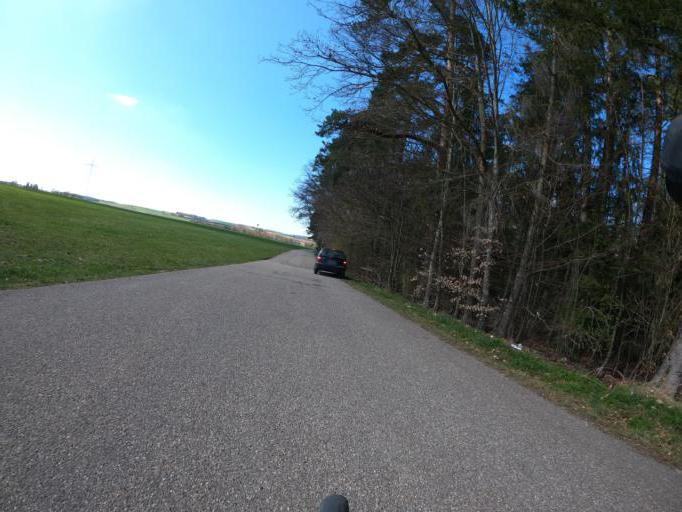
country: DE
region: Baden-Wuerttemberg
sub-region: Karlsruhe Region
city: Horb am Neckar
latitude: 48.4326
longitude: 8.7248
